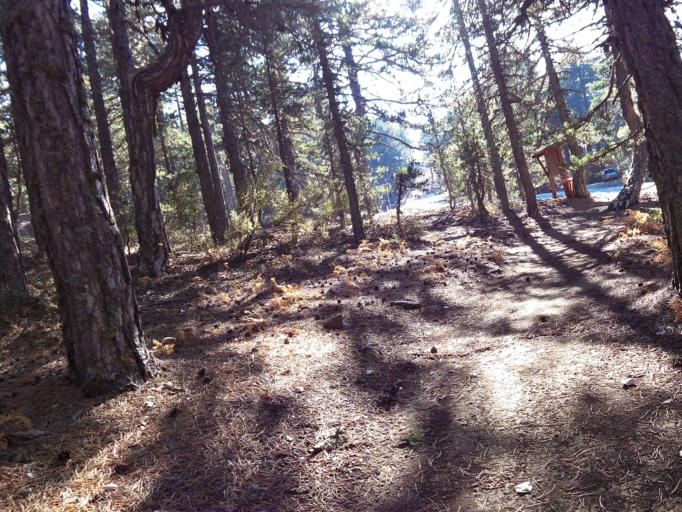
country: CY
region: Lefkosia
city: Kakopetria
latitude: 34.9479
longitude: 32.8475
